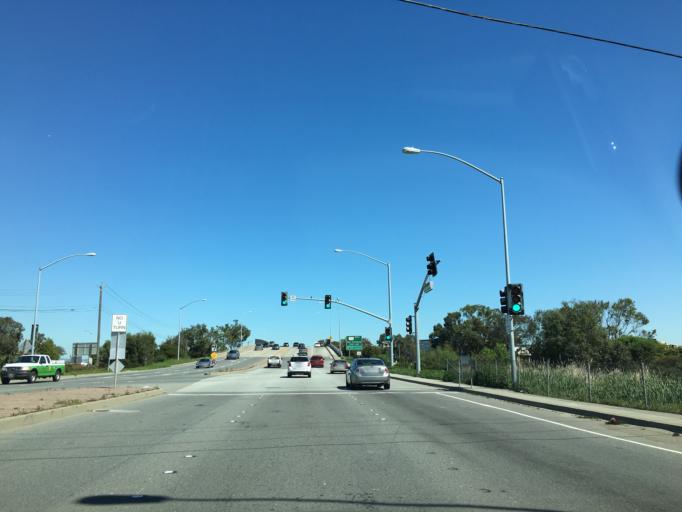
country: US
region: California
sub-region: San Mateo County
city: Millbrae
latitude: 37.6012
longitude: -122.3827
